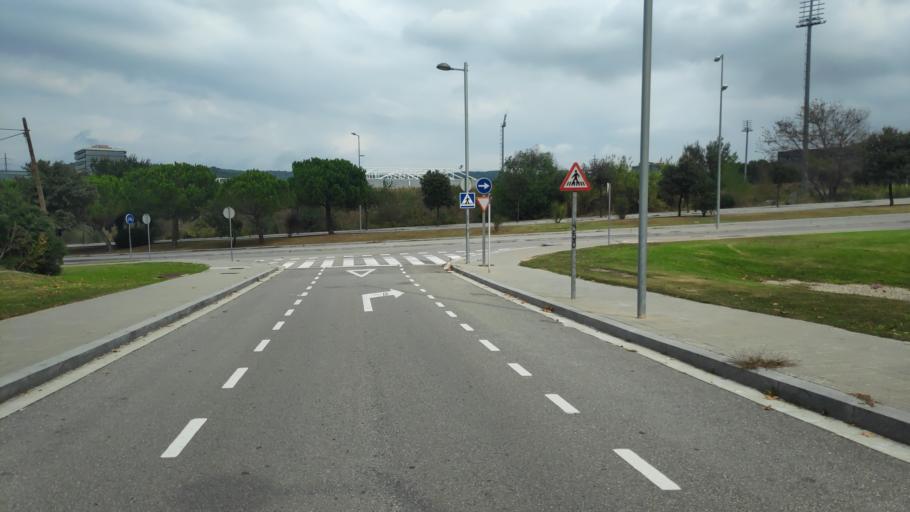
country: ES
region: Catalonia
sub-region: Provincia de Barcelona
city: Rubi
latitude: 41.4821
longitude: 2.0591
